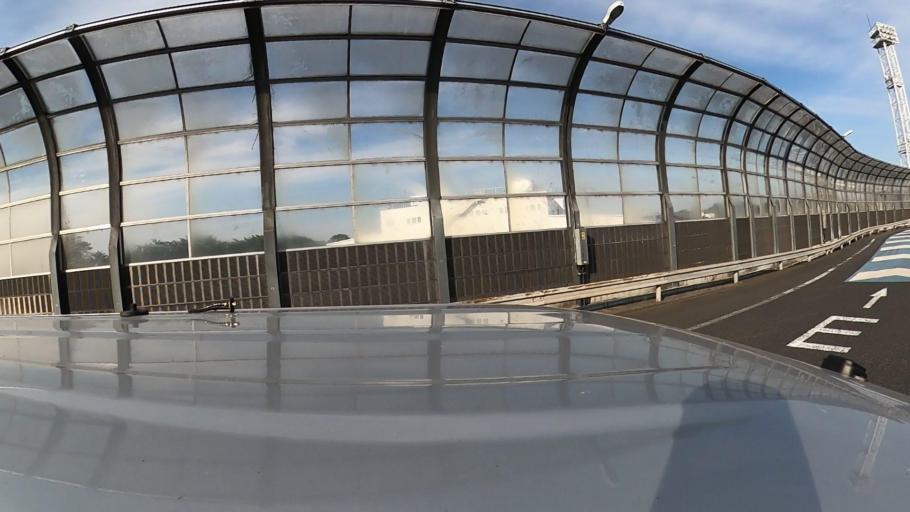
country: JP
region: Saitama
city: Asaka
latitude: 35.7752
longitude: 139.5680
